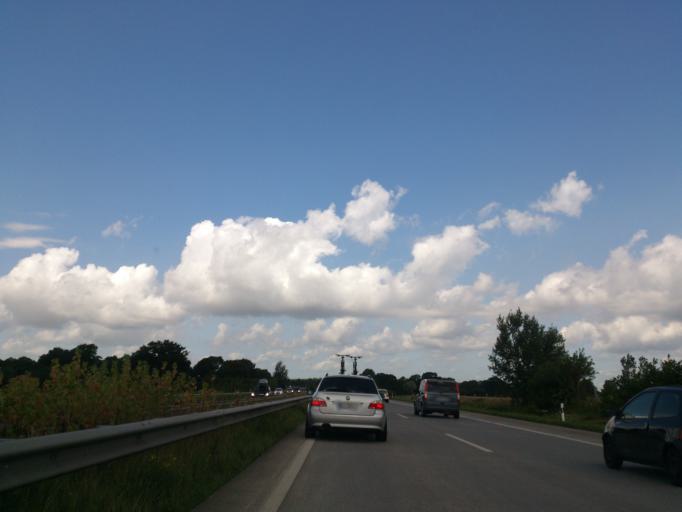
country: DE
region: Schleswig-Holstein
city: Neuenbrook
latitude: 53.8811
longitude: 9.5484
